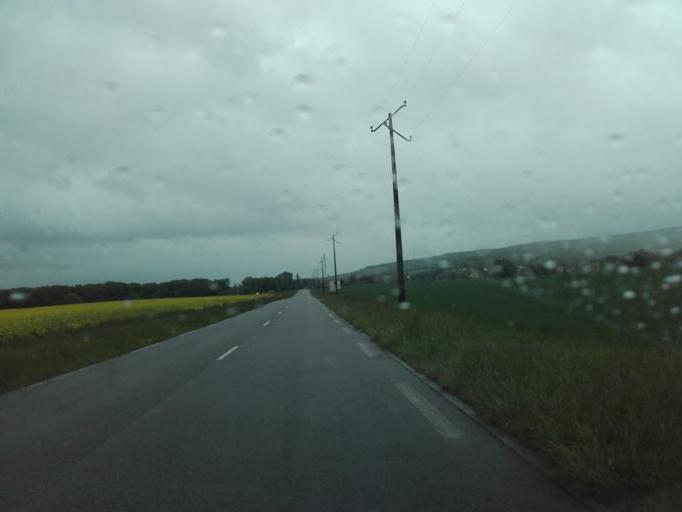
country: FR
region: Bourgogne
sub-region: Departement de Saone-et-Loire
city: Mellecey
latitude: 46.8268
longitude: 4.7521
